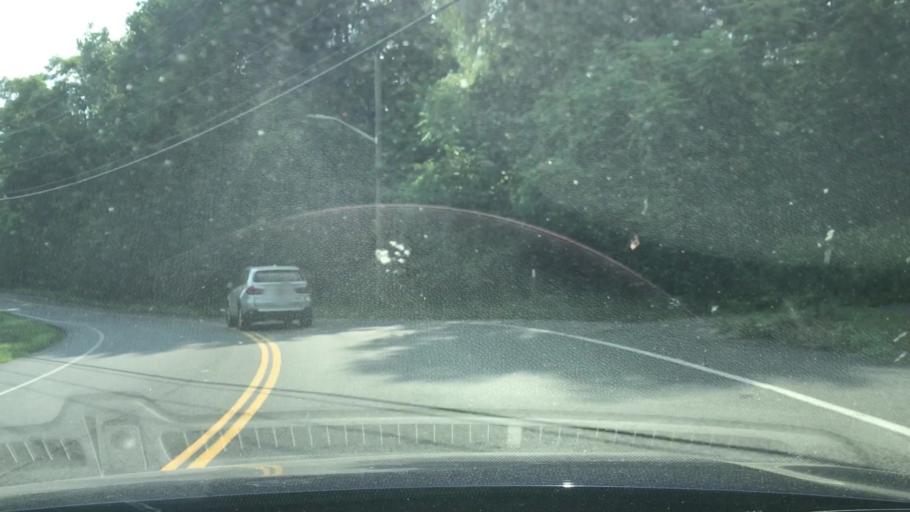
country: US
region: New York
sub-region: Rockland County
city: Bardonia
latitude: 41.1121
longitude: -74.0190
